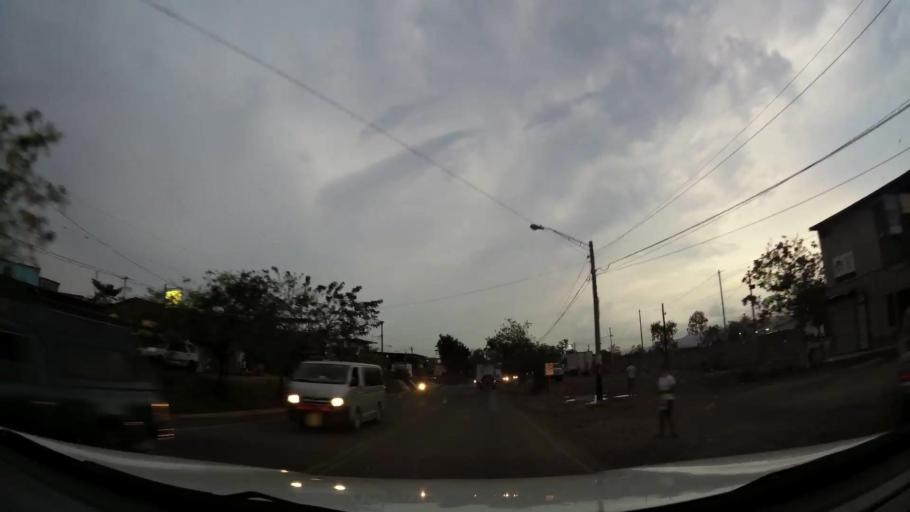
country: NI
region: Esteli
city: Esteli
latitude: 13.0746
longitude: -86.3526
